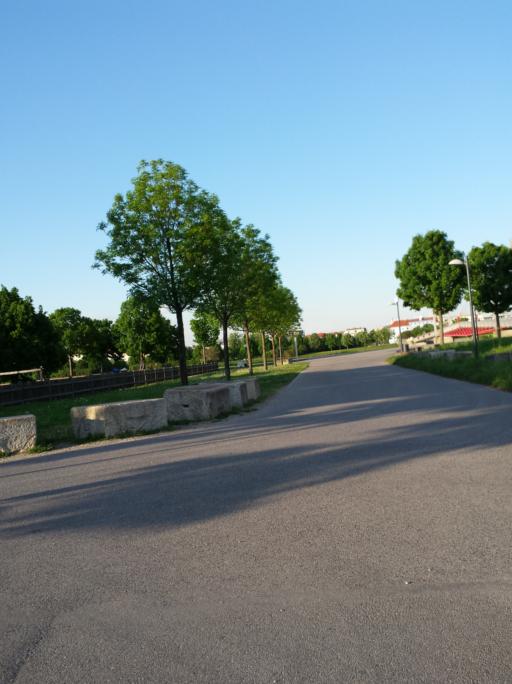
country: AT
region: Vienna
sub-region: Wien Stadt
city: Vienna
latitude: 48.2217
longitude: 16.4175
